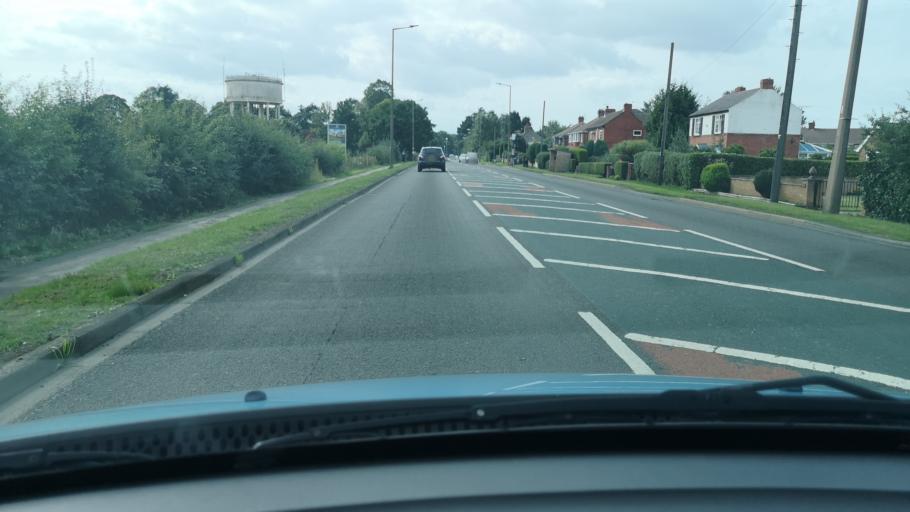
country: GB
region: England
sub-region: Doncaster
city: Hatfield
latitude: 53.5680
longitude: -1.0142
